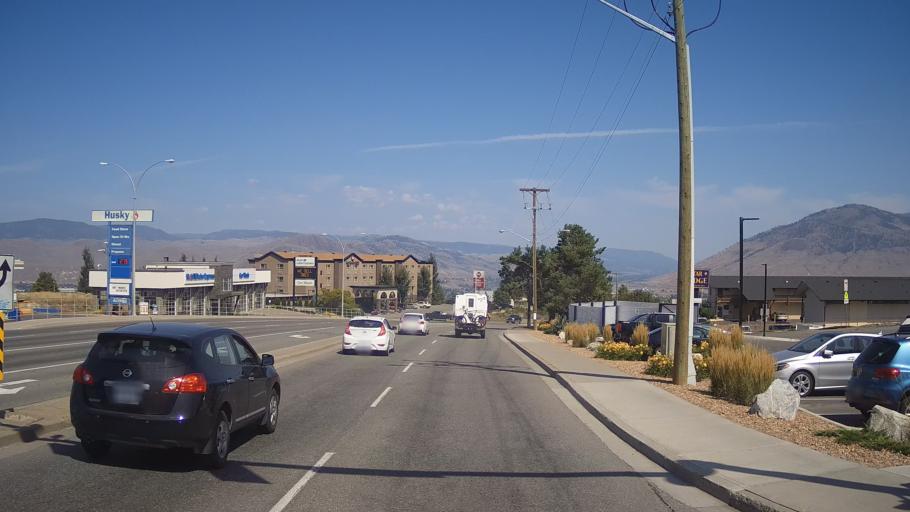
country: CA
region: British Columbia
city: Kamloops
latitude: 50.6699
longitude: -120.3544
